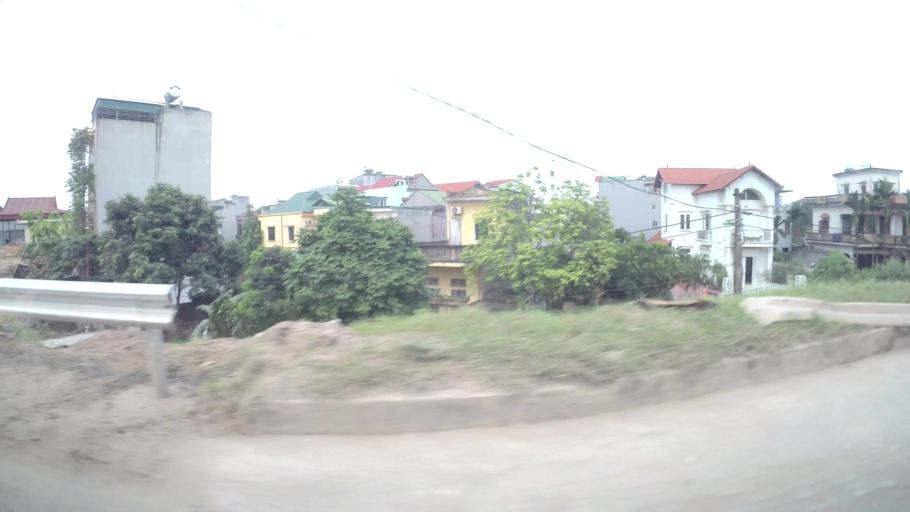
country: VN
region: Ha Noi
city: Trau Quy
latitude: 21.0622
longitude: 105.9198
